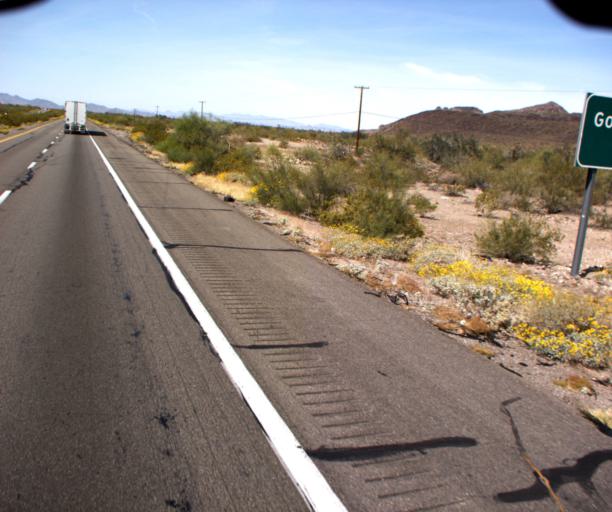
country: US
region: Arizona
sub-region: La Paz County
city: Quartzsite
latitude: 33.6783
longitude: -114.0651
